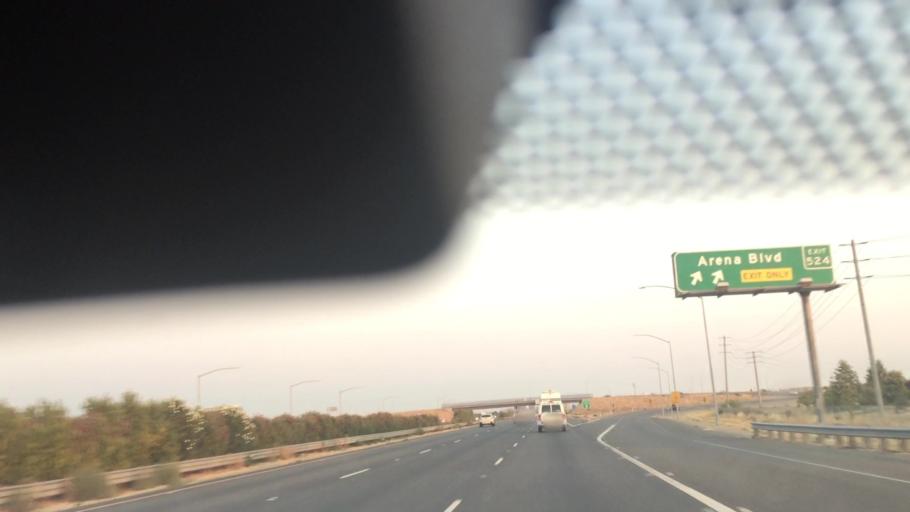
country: US
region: California
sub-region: Yolo County
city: West Sacramento
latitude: 38.6477
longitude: -121.5289
